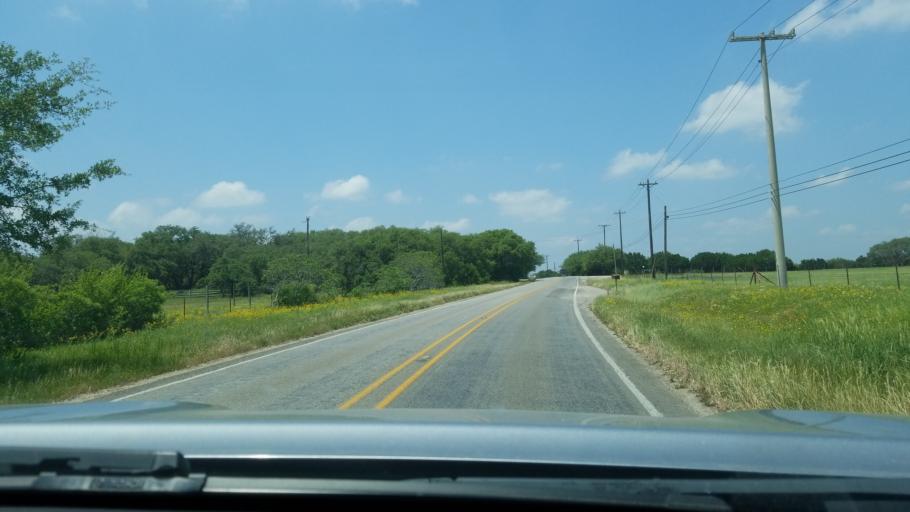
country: US
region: Texas
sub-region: Hays County
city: Woodcreek
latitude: 30.0262
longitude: -98.1653
